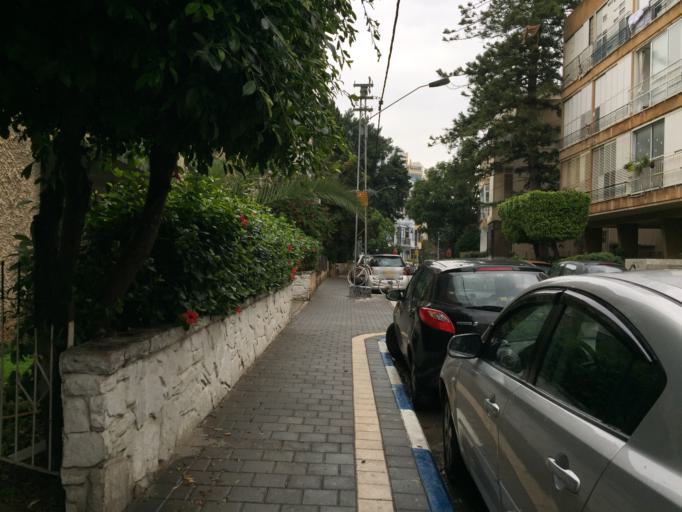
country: IL
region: Tel Aviv
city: Tel Aviv
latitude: 32.0705
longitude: 34.7743
